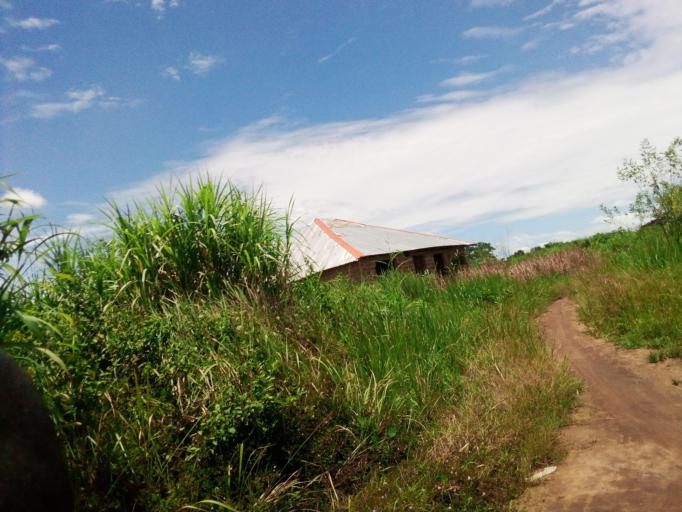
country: SL
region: Eastern Province
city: Koidu
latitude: 8.6423
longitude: -10.9280
